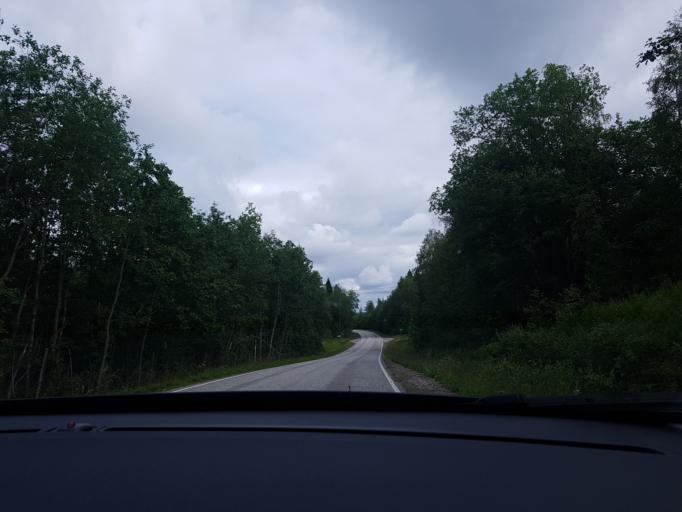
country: FI
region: Kainuu
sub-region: Kehys-Kainuu
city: Kuhmo
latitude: 64.2114
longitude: 29.4458
